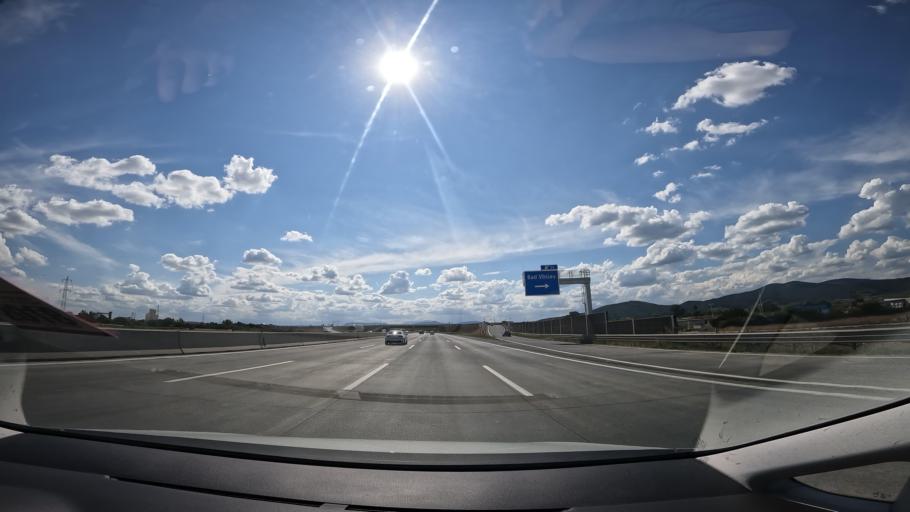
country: AT
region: Lower Austria
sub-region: Politischer Bezirk Baden
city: Gunselsdorf
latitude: 47.9694
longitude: 16.2501
